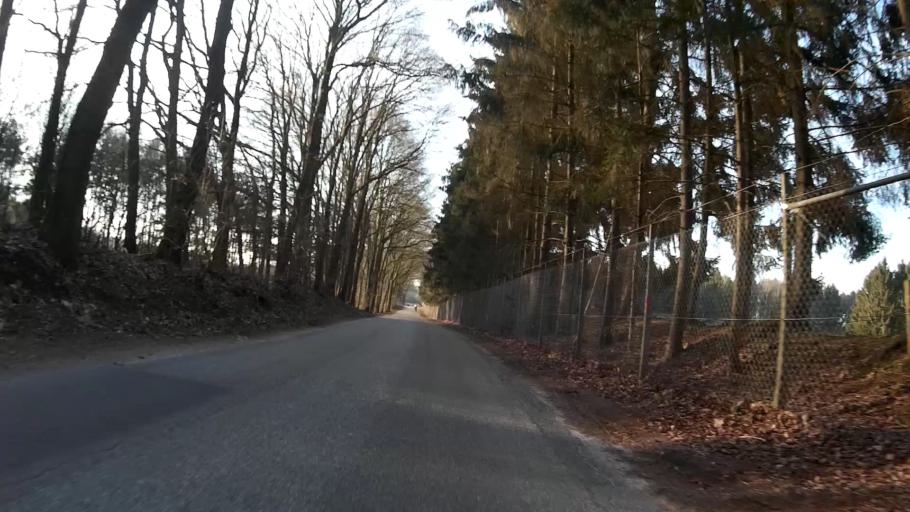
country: NL
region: Utrecht
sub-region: Gemeente Veenendaal
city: Veenendaal
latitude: 51.9932
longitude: 5.5562
